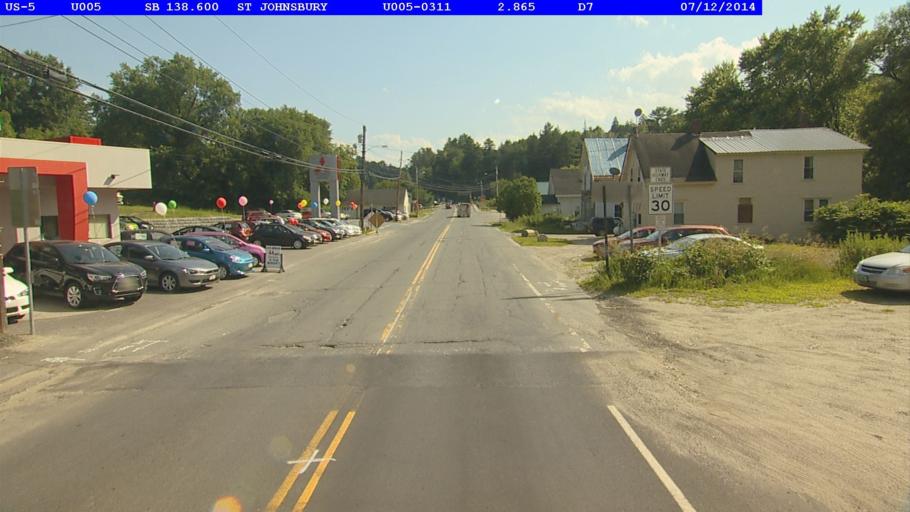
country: US
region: Vermont
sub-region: Caledonia County
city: St Johnsbury
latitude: 44.4335
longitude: -72.0170
